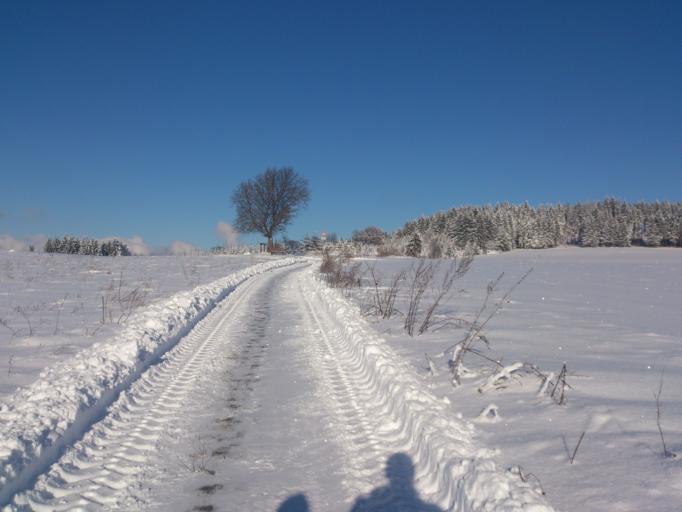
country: DE
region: Bavaria
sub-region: Upper Franconia
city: Rugendorf
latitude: 50.1955
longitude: 11.4979
